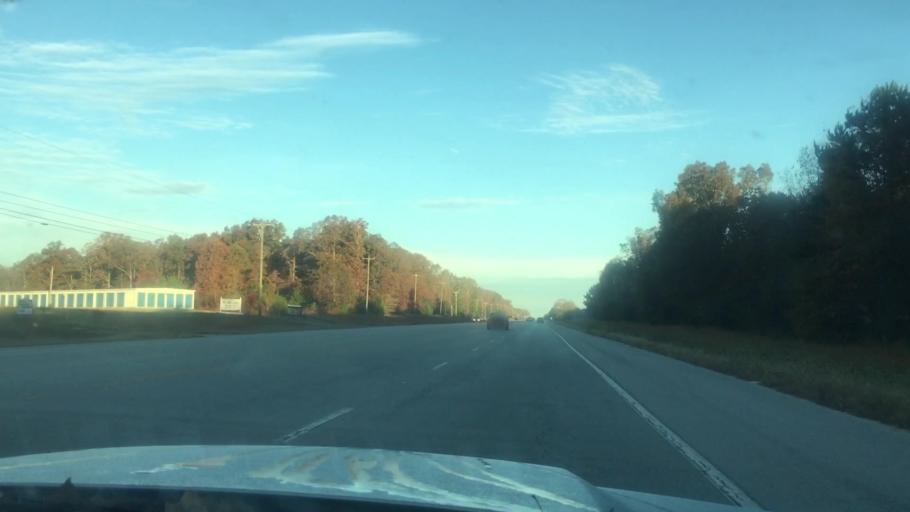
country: US
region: Tennessee
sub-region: Franklin County
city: Estill Springs
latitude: 35.3014
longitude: -86.1550
